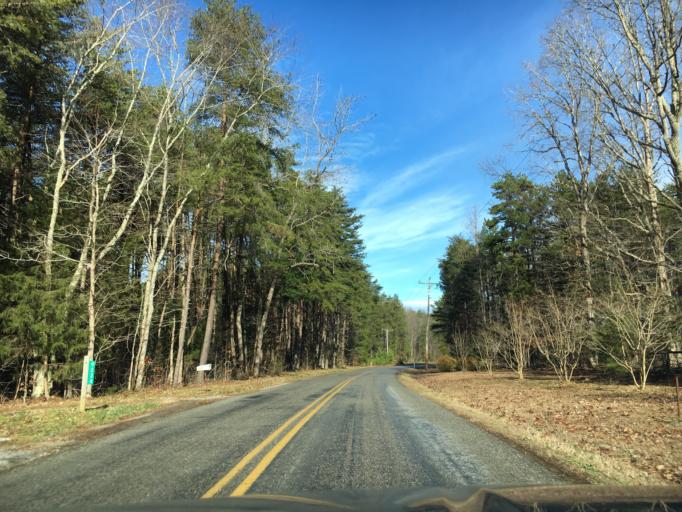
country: US
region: Virginia
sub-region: Nottoway County
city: Crewe
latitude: 37.3417
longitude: -78.1598
